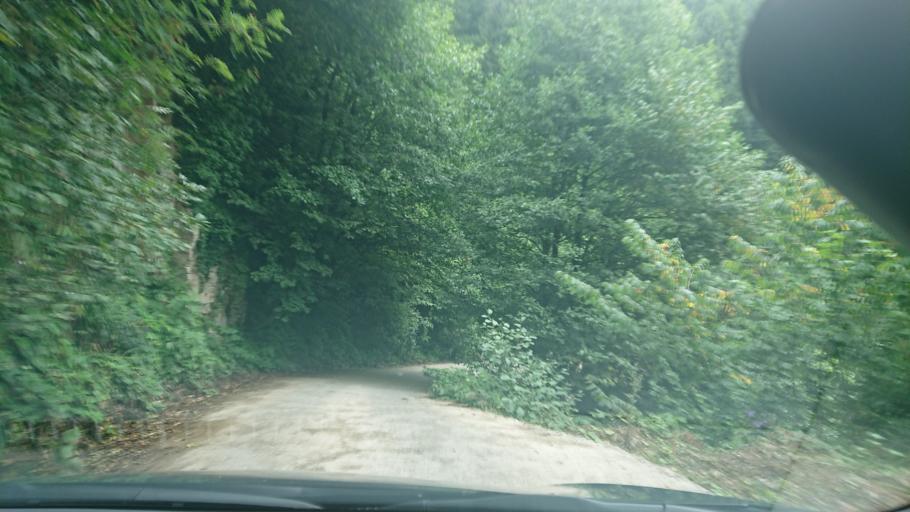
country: TR
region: Gumushane
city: Kurtun
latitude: 40.6699
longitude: 39.0392
